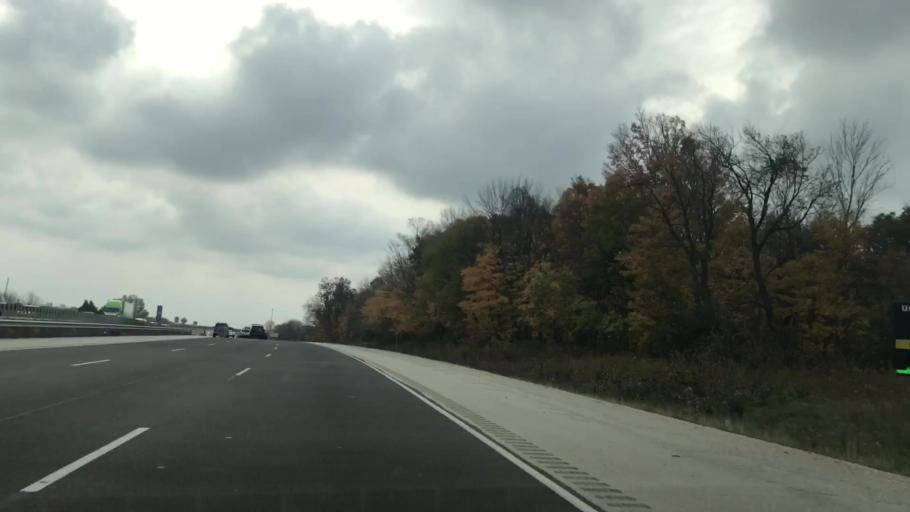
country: US
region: Wisconsin
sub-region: Washington County
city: Richfield
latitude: 43.2405
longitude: -88.1794
